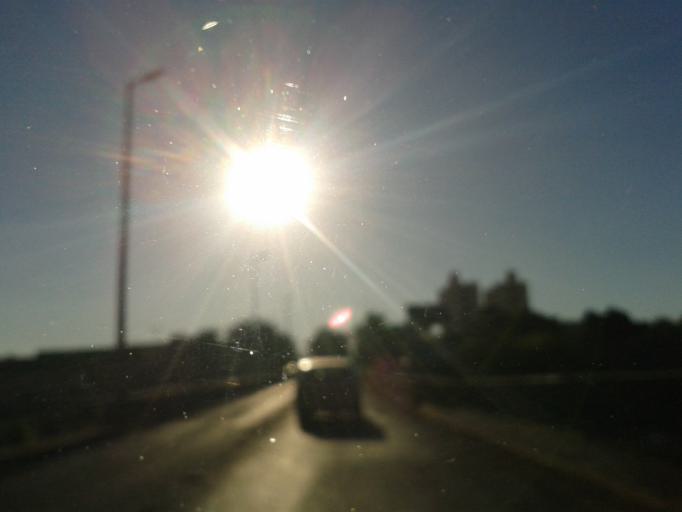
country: BR
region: Minas Gerais
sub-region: Uberlandia
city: Uberlandia
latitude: -18.8955
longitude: -48.2712
